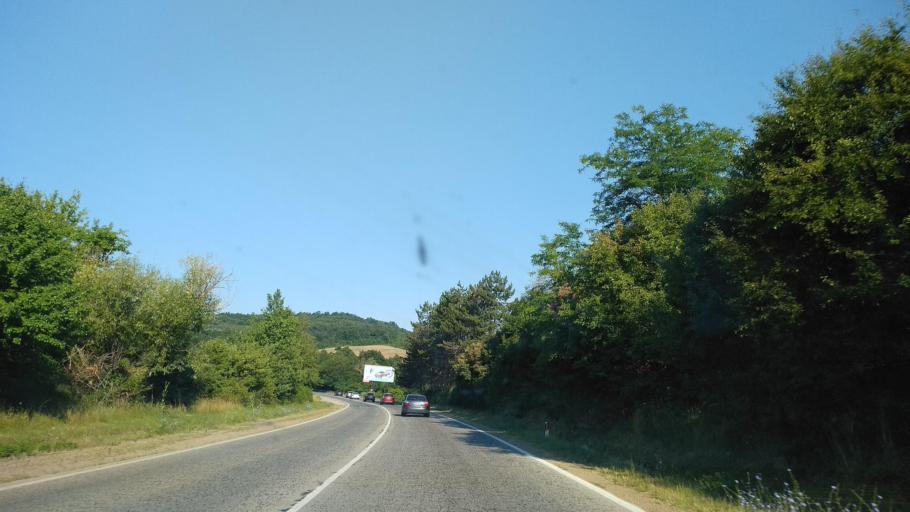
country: BG
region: Lovech
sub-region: Obshtina Lovech
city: Lovech
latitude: 43.0487
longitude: 24.8646
